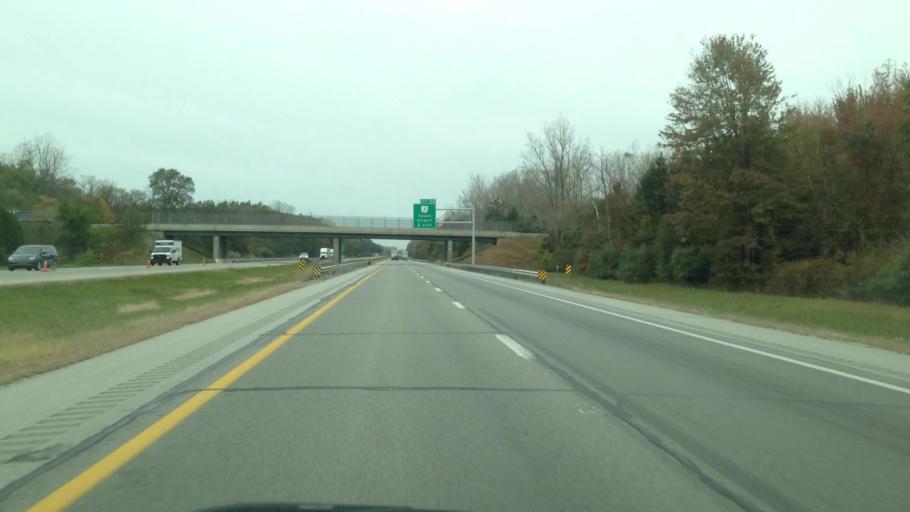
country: US
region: Ohio
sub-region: Lucas County
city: Holland
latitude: 41.5927
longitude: -83.7593
